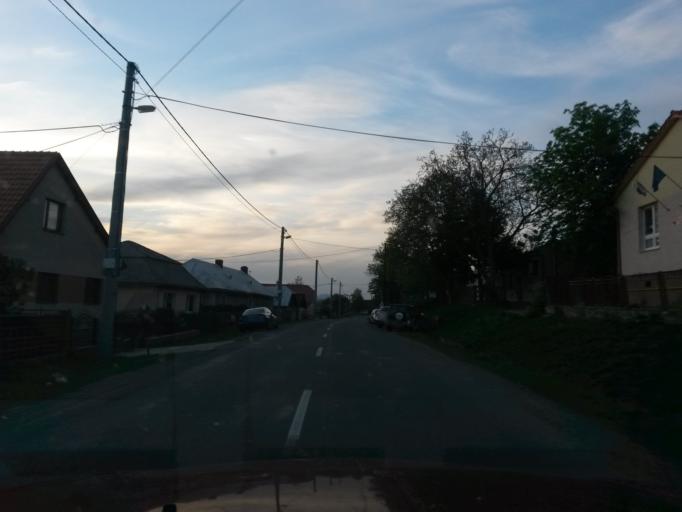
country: HU
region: Borsod-Abauj-Zemplen
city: Satoraljaujhely
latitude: 48.4889
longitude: 21.6372
